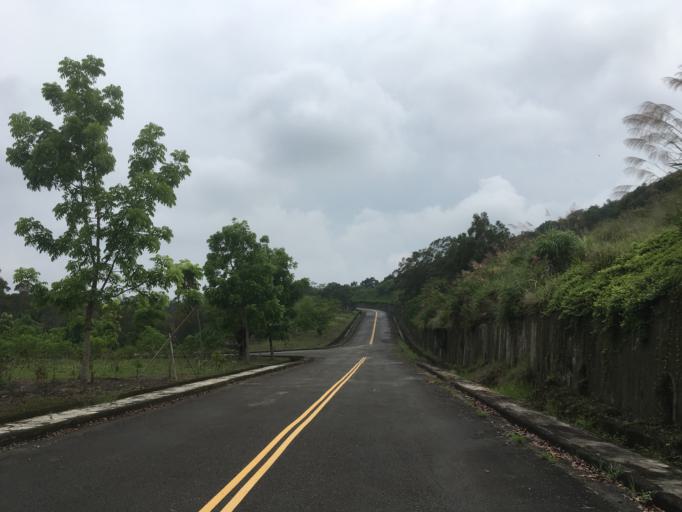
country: TW
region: Taiwan
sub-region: Taichung City
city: Taichung
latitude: 24.1681
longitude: 120.7740
